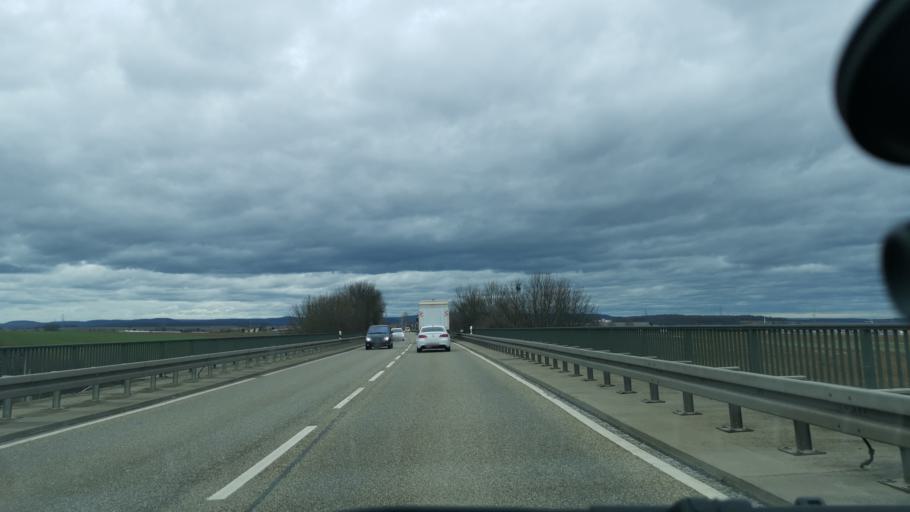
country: DE
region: Baden-Wuerttemberg
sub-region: Regierungsbezirk Stuttgart
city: Schwieberdingen
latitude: 48.8871
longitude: 9.0932
